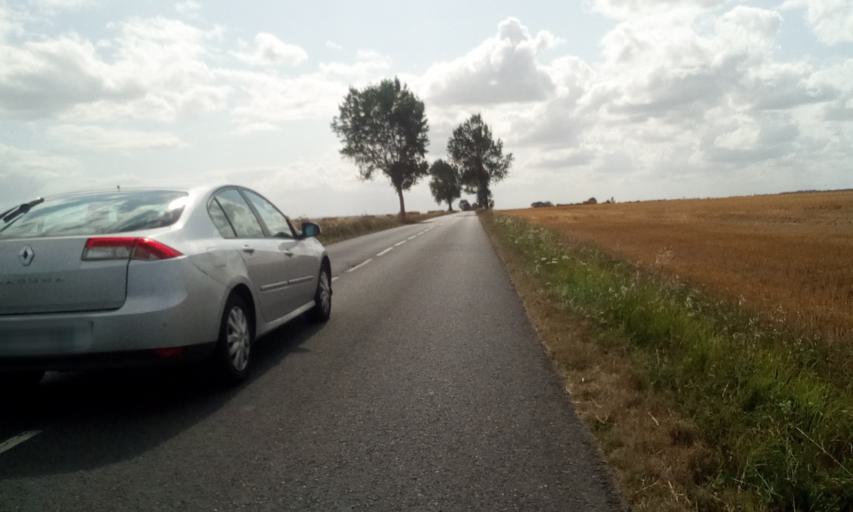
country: FR
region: Lower Normandy
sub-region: Departement du Calvados
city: Ver-sur-Mer
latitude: 49.3062
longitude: -0.5030
